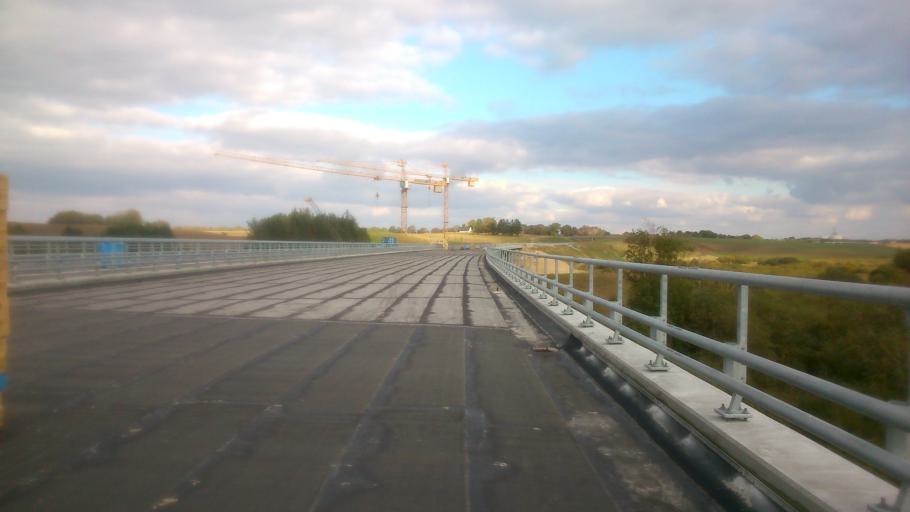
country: DK
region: Central Jutland
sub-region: Silkeborg Kommune
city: Silkeborg
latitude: 56.2034
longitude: 9.5214
